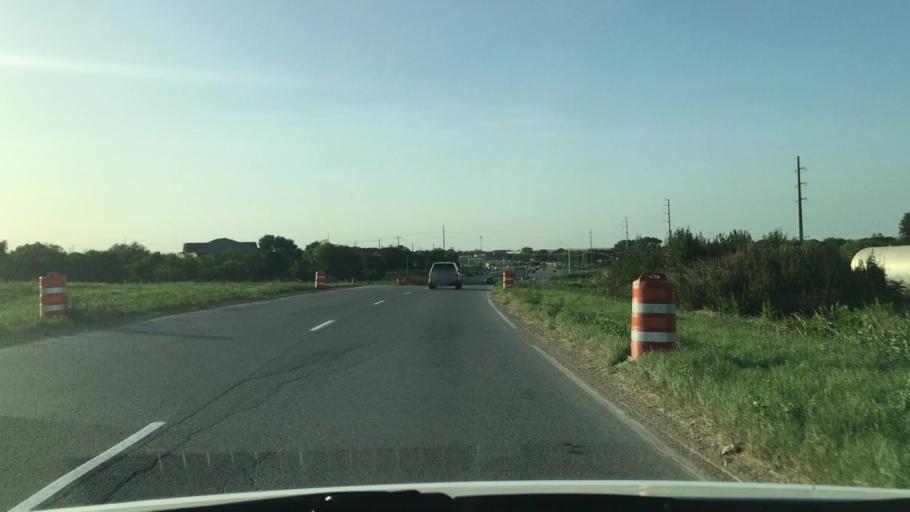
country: US
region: Texas
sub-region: Travis County
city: Austin
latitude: 30.2266
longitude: -97.6819
